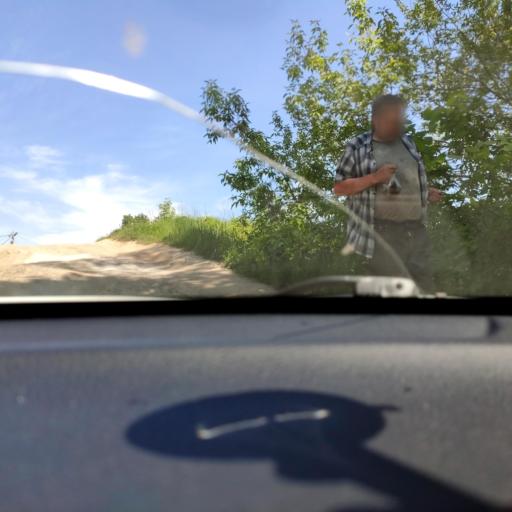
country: RU
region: Tatarstan
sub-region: Gorod Kazan'
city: Kazan
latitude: 55.8640
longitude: 49.1951
